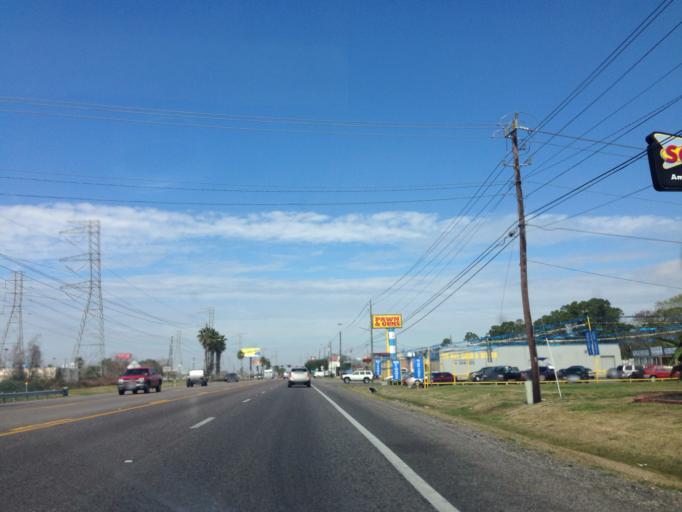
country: US
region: Texas
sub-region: Galveston County
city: Kemah
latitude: 29.5353
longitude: -95.0164
